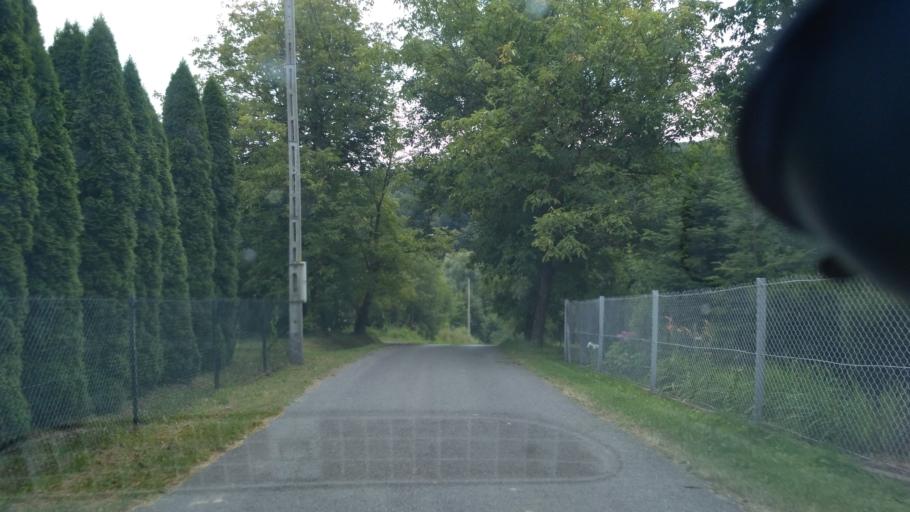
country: PL
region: Subcarpathian Voivodeship
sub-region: Powiat przeworski
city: Lopuszka Wielka
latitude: 49.8984
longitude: 22.4206
